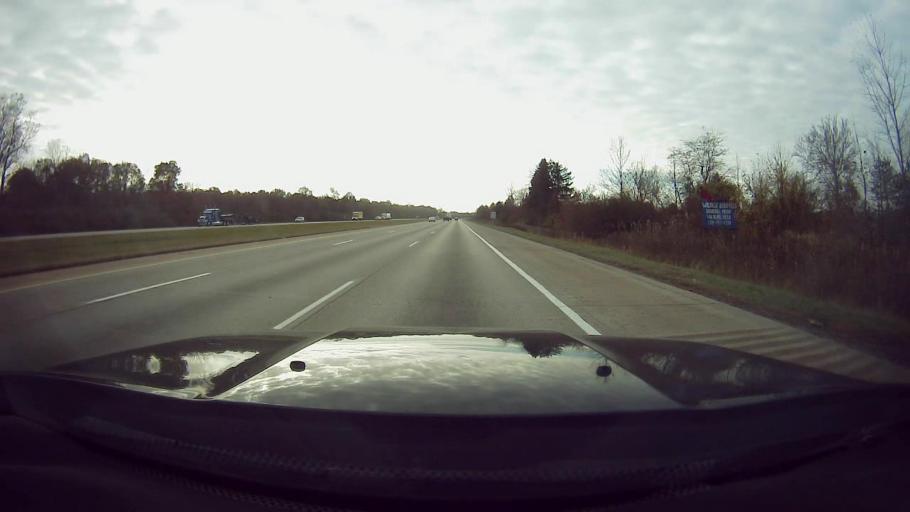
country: US
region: Michigan
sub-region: Monroe County
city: Carleton
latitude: 42.1236
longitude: -83.3806
